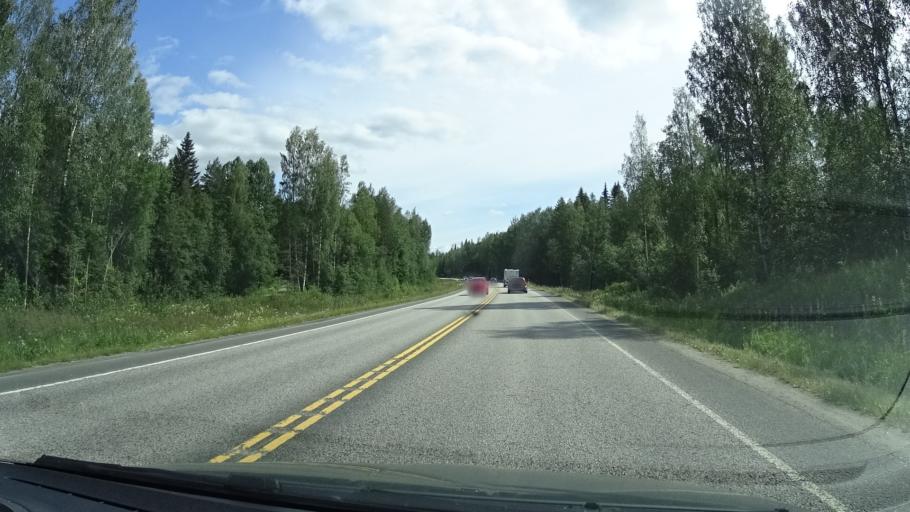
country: FI
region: Central Finland
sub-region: Jyvaeskylae
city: Jyvaeskylae
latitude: 62.2656
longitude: 25.5634
